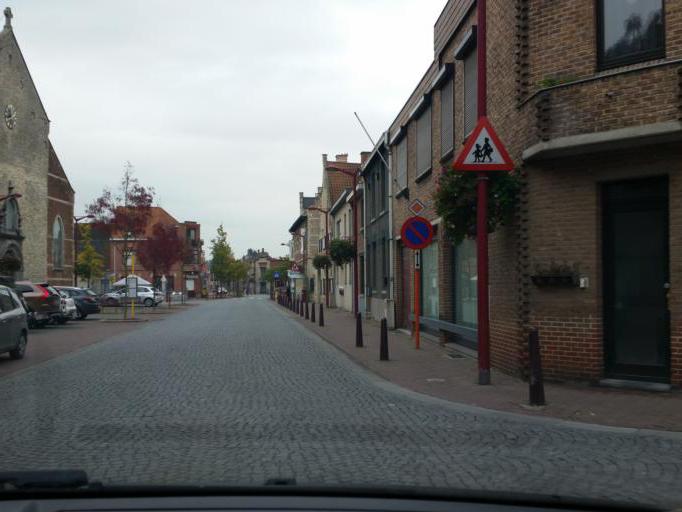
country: BE
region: Flanders
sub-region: Provincie Vlaams-Brabant
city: Steenokkerzeel
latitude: 50.9337
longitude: 4.4965
